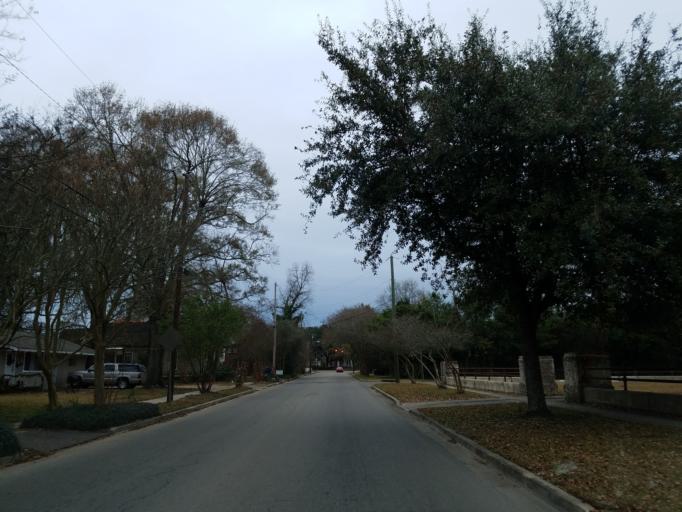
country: US
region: Mississippi
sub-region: Forrest County
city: Hattiesburg
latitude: 31.3237
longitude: -89.2843
